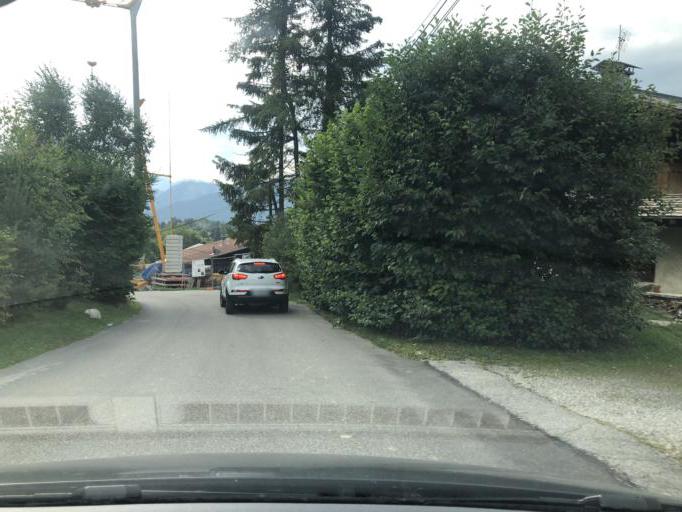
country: FR
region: Rhone-Alpes
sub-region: Departement de la Haute-Savoie
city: Megeve
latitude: 45.8452
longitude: 6.6413
